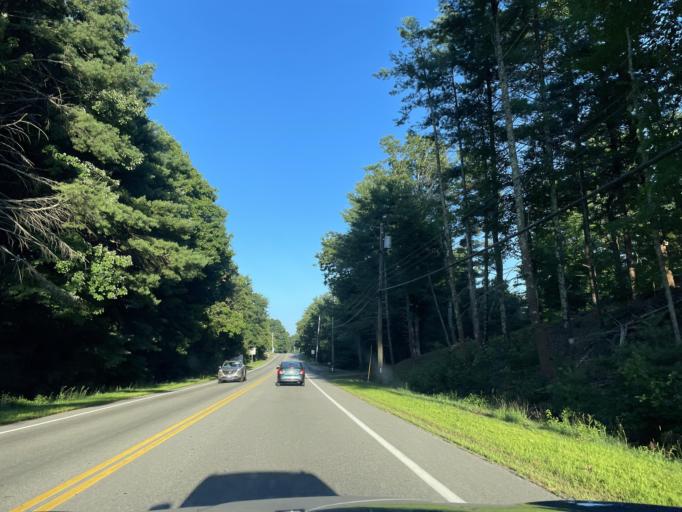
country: US
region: Massachusetts
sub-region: Plymouth County
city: Halifax
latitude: 41.9949
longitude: -70.8802
